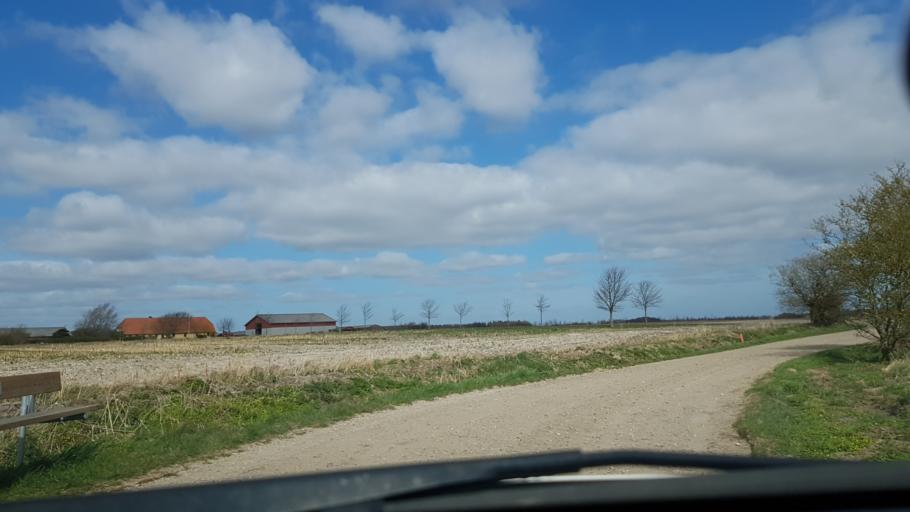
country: DK
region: South Denmark
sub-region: Esbjerg Kommune
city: Ribe
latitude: 55.2512
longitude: 8.8377
